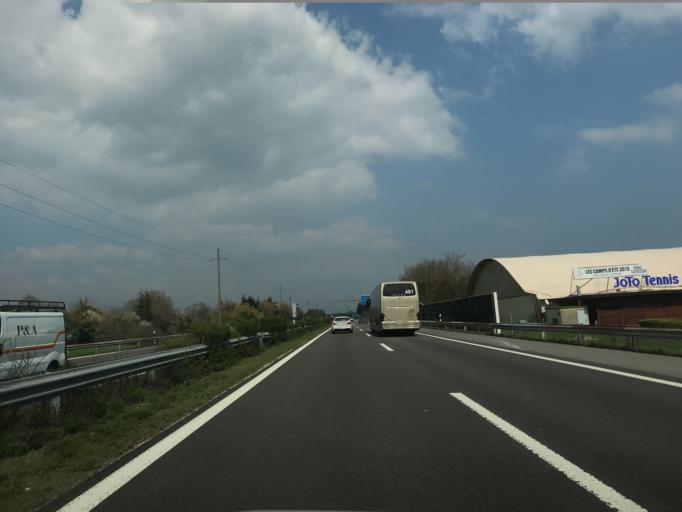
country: CH
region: Vaud
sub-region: Nyon District
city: Founex
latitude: 46.3348
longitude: 6.1591
